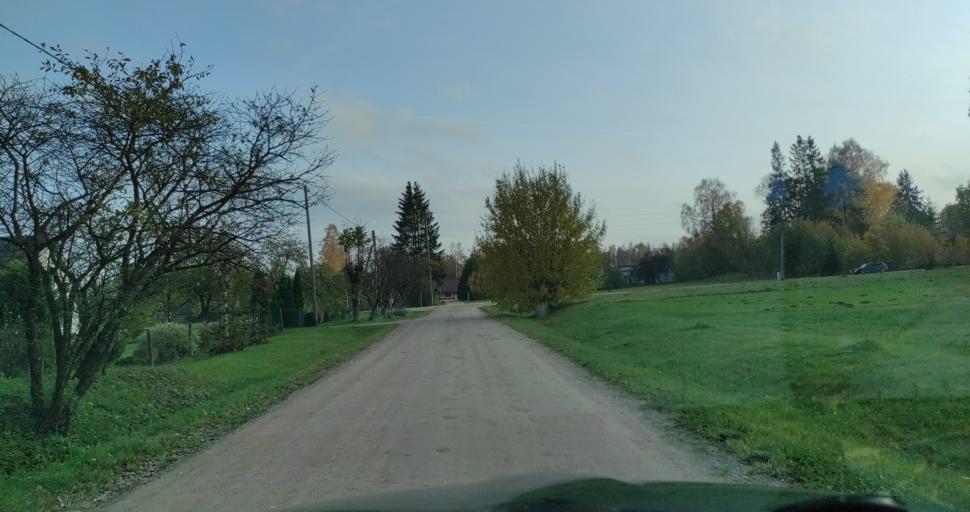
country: LV
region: Vainode
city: Vainode
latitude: 56.4233
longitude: 21.8747
